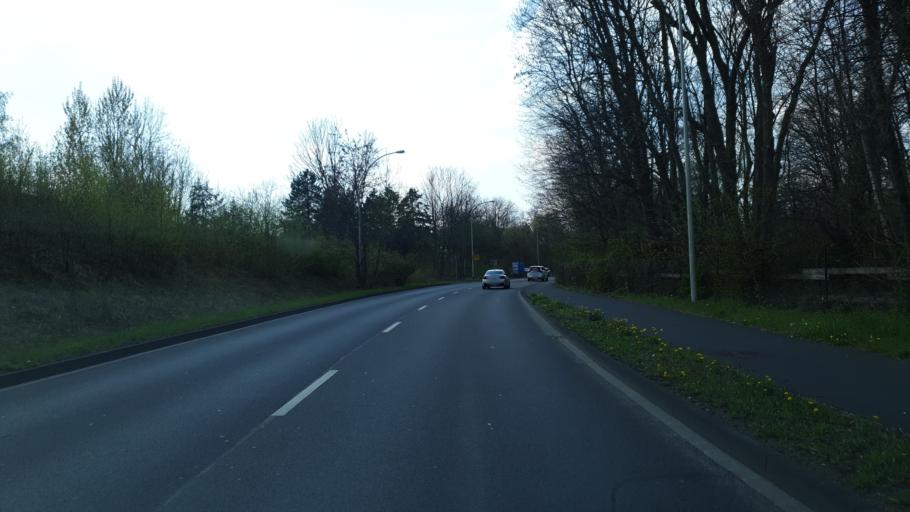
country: DE
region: North Rhine-Westphalia
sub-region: Regierungsbezirk Koln
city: Frechen
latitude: 50.9025
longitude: 6.7936
